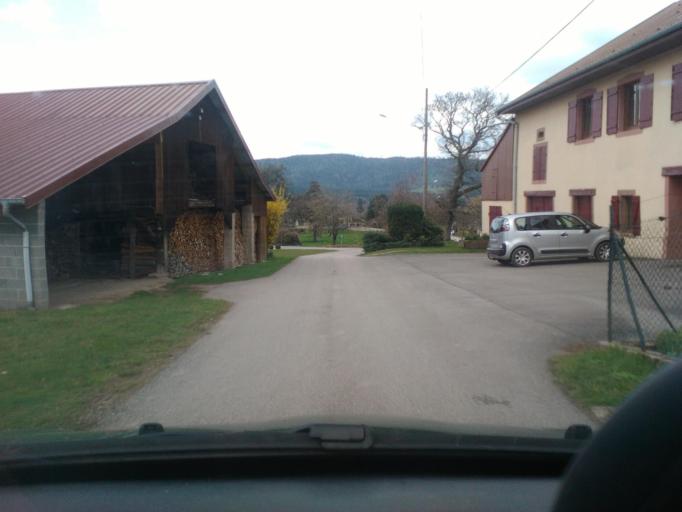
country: FR
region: Lorraine
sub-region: Departement des Vosges
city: Etival-Clairefontaine
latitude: 48.3485
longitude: 6.8289
